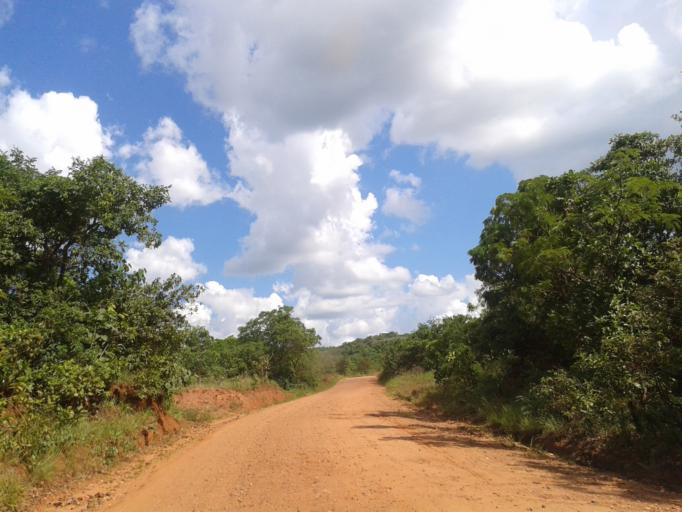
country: BR
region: Minas Gerais
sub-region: Campina Verde
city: Campina Verde
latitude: -19.3189
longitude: -49.8036
